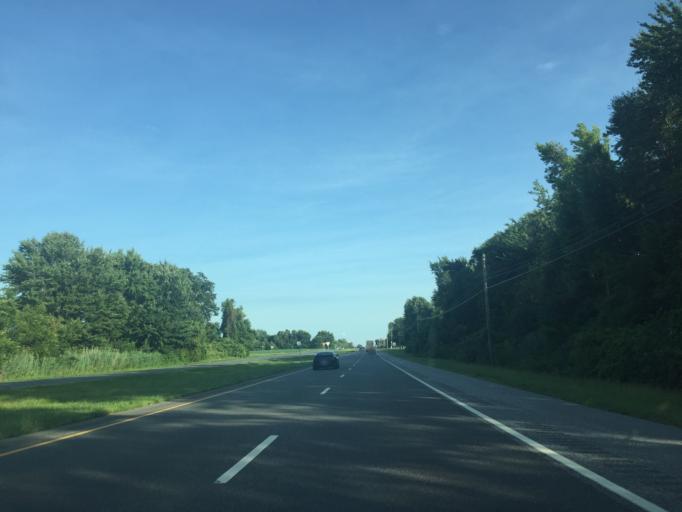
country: US
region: Delaware
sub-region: Kent County
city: Cheswold
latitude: 39.2390
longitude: -75.5851
